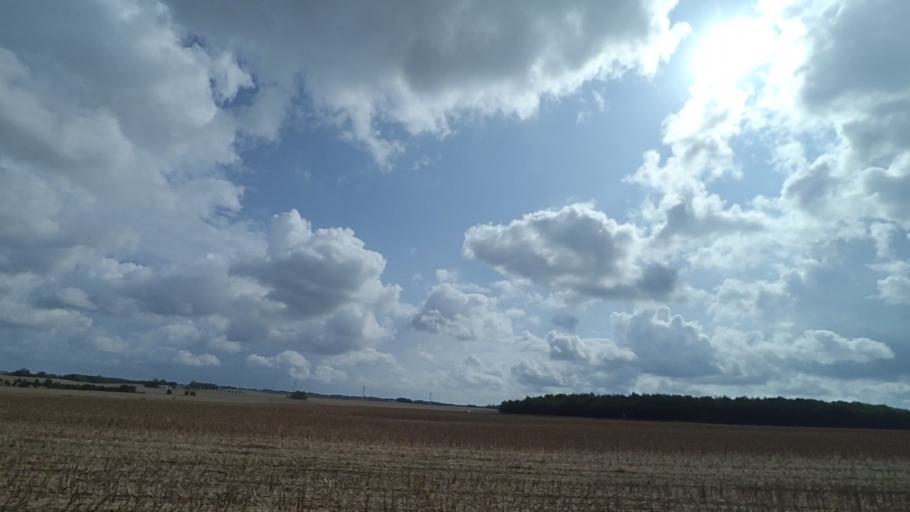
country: DK
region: Central Jutland
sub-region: Norddjurs Kommune
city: Auning
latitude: 56.4899
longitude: 10.4432
